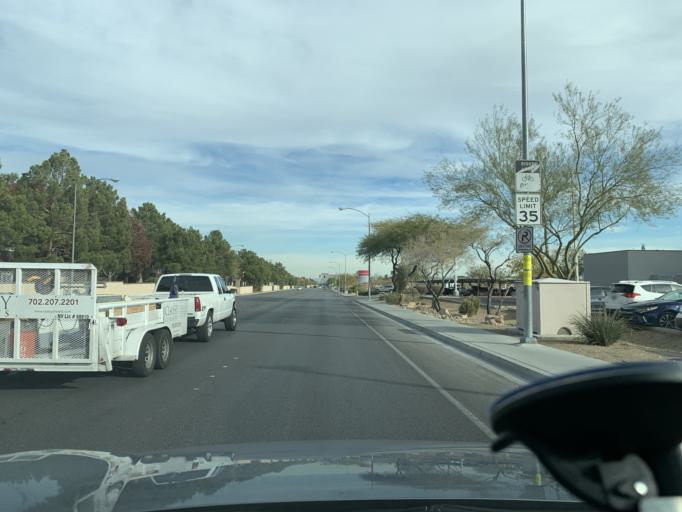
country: US
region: Nevada
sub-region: Clark County
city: Spring Valley
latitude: 36.0924
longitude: -115.2423
